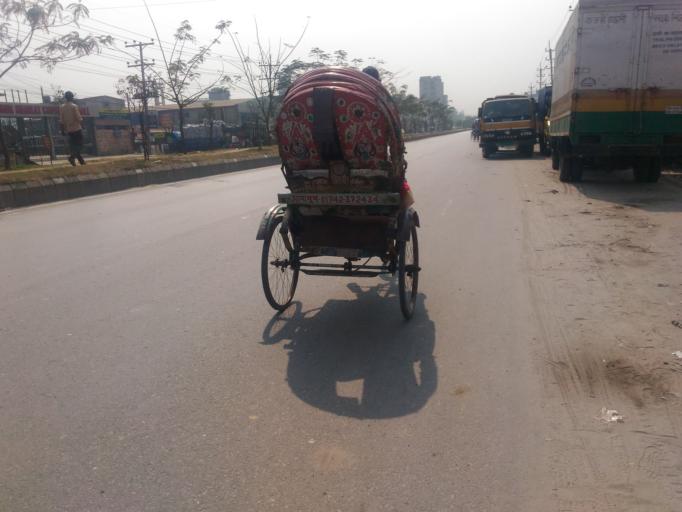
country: BD
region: Dhaka
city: Tungi
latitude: 24.0040
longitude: 90.3831
